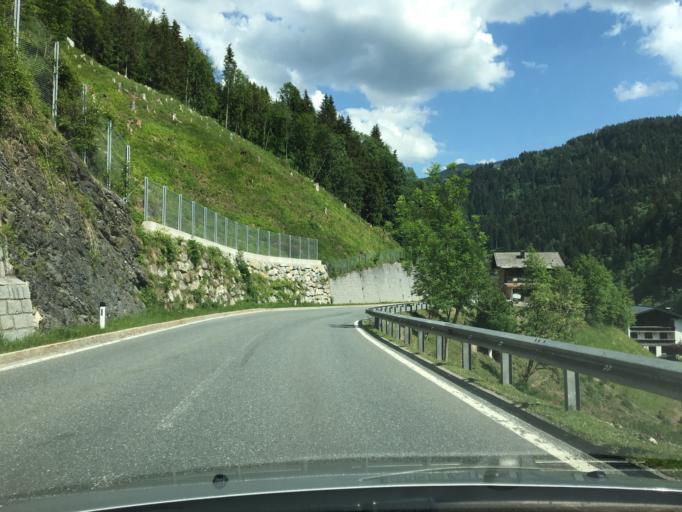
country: AT
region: Salzburg
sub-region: Politischer Bezirk Sankt Johann im Pongau
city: Sankt Johann im Pongau
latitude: 47.3334
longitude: 13.2229
